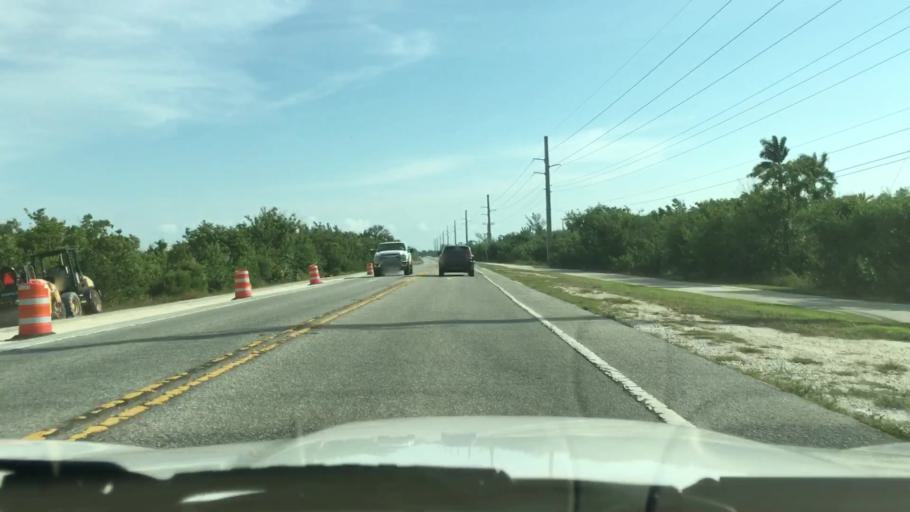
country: US
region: Florida
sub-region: Monroe County
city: Cudjoe Key
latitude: 24.6631
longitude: -81.5116
